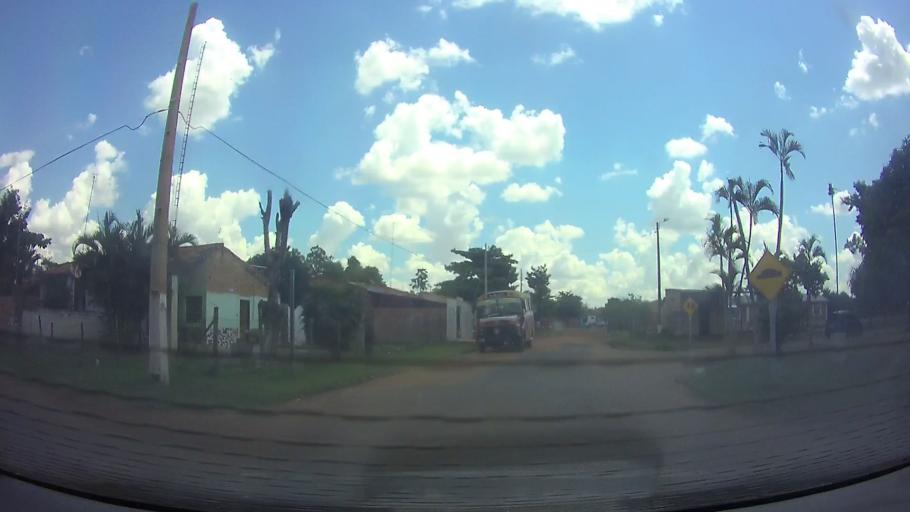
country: PY
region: Central
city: Limpio
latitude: -25.1657
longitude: -57.4288
